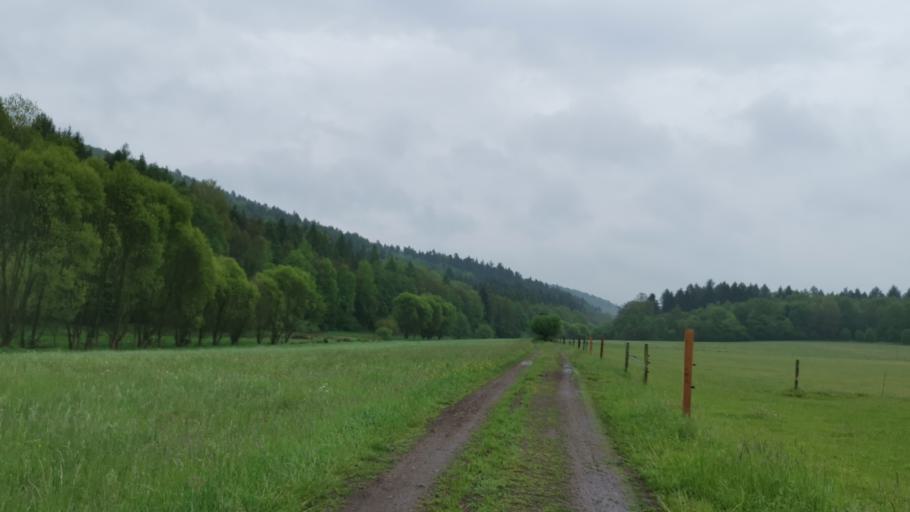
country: DE
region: Saarland
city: Kirkel
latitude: 49.2705
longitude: 7.1876
